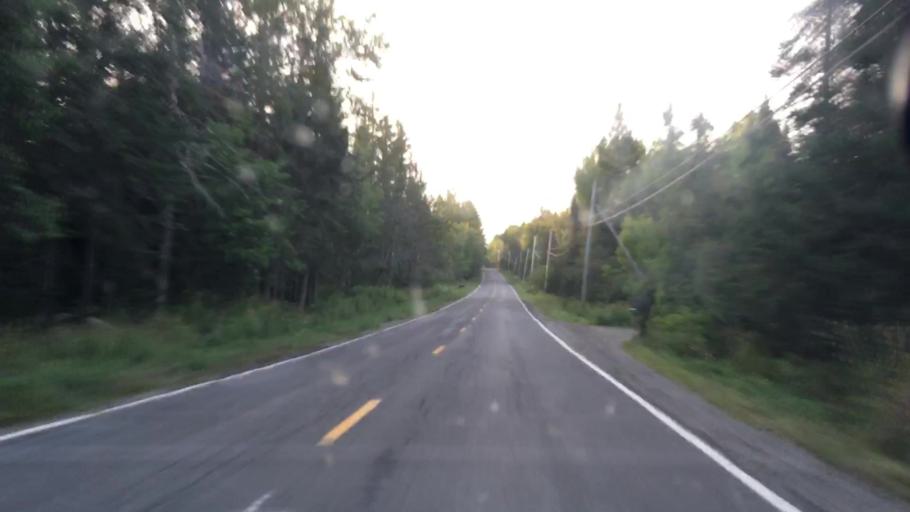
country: US
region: Maine
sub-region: Penobscot County
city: Hermon
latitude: 44.7034
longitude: -68.9472
